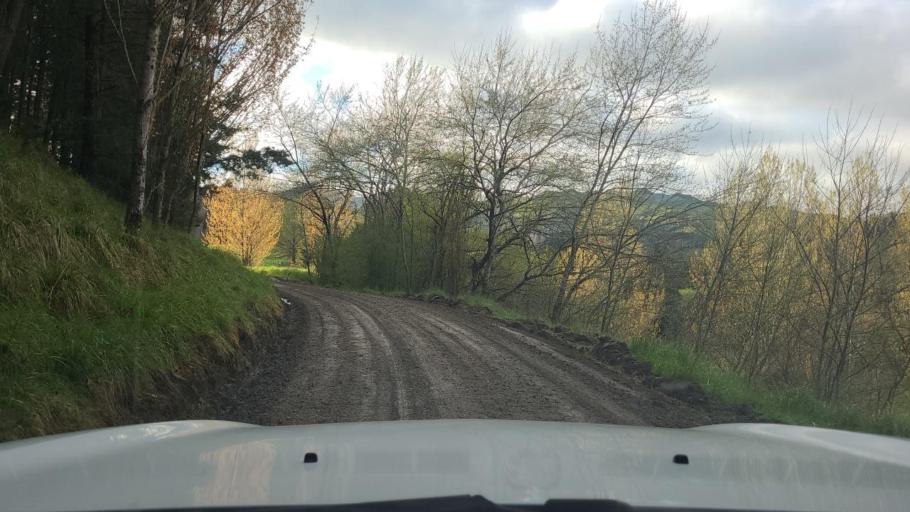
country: NZ
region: Wellington
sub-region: South Wairarapa District
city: Waipawa
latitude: -41.2225
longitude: 175.6824
